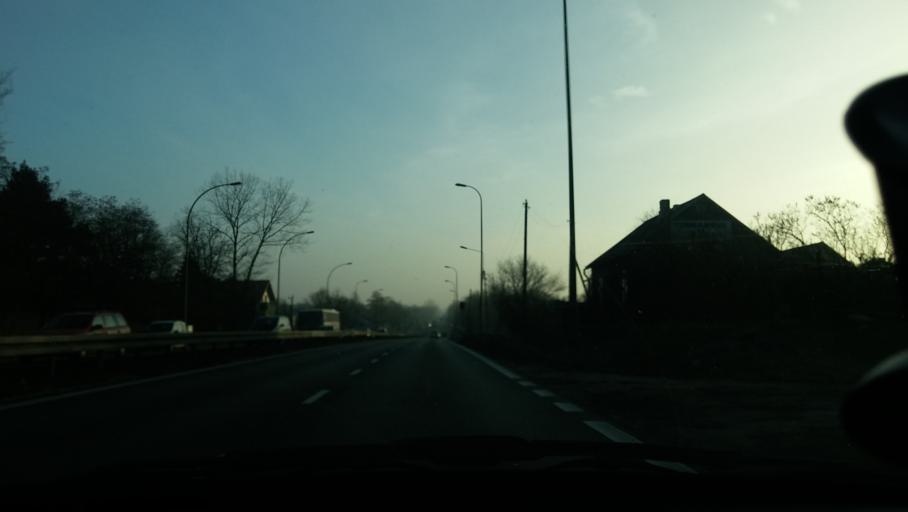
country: PL
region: Masovian Voivodeship
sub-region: Warszawa
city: Wesola
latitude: 52.2240
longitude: 21.2173
